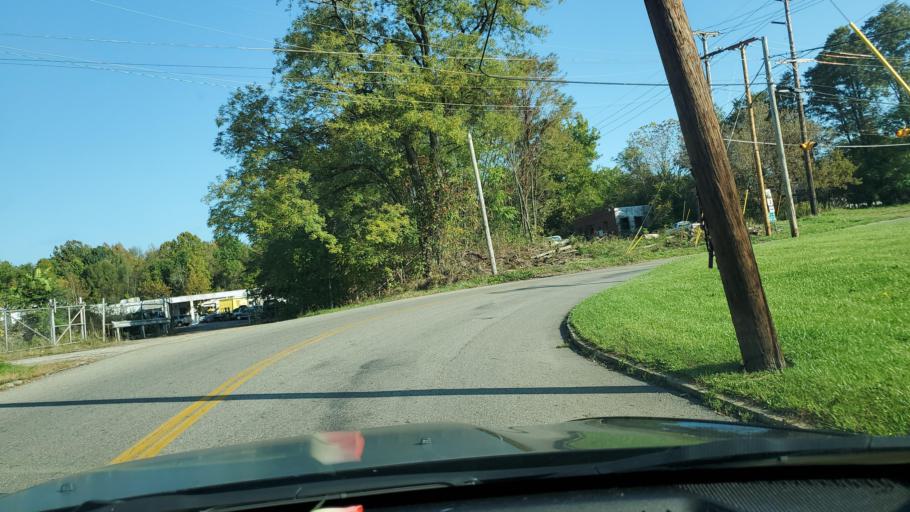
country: US
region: Ohio
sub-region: Mahoning County
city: Youngstown
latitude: 41.1234
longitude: -80.6321
